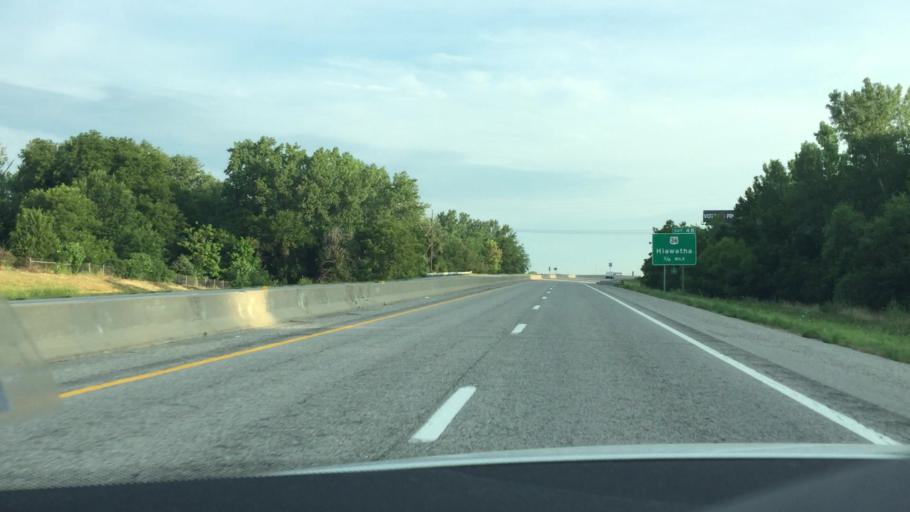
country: US
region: Kansas
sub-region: Doniphan County
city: Elwood
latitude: 39.7341
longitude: -94.8489
